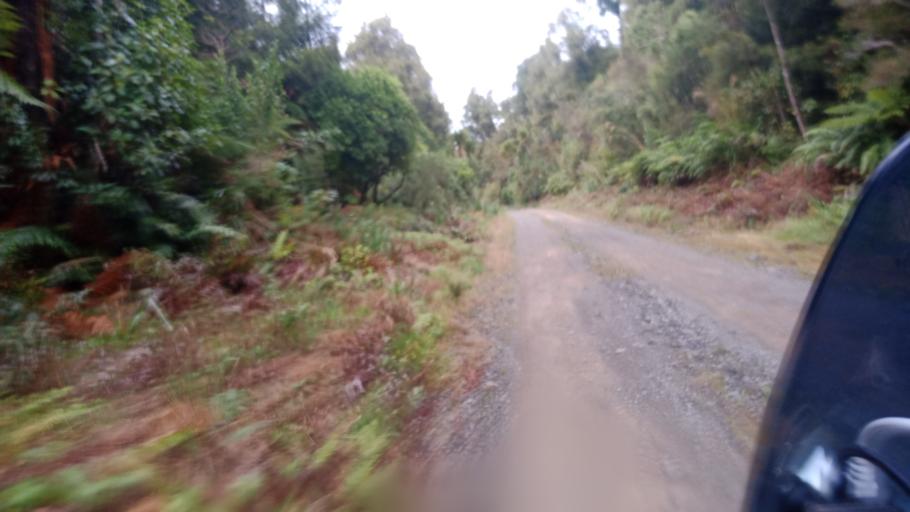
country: NZ
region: Bay of Plenty
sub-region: Whakatane District
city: Murupara
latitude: -38.6850
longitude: 176.6068
